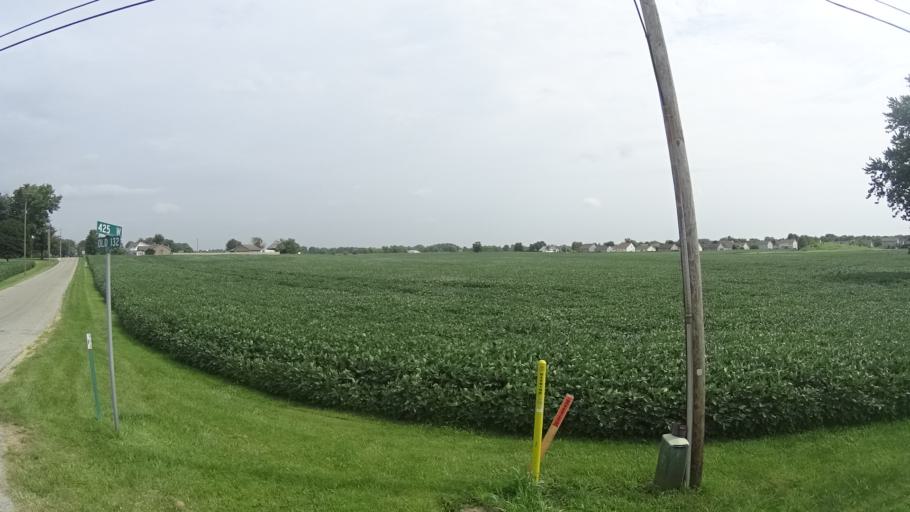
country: US
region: Indiana
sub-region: Madison County
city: Pendleton
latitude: 40.0103
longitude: -85.7534
